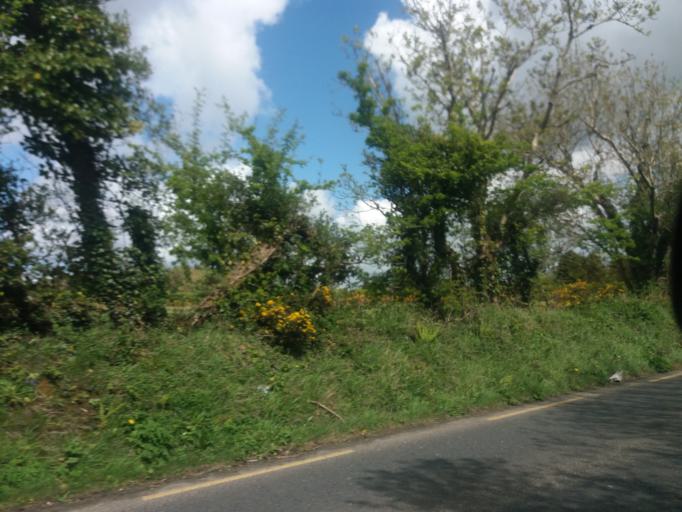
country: IE
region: Leinster
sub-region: Loch Garman
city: Loch Garman
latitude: 52.3159
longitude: -6.5237
